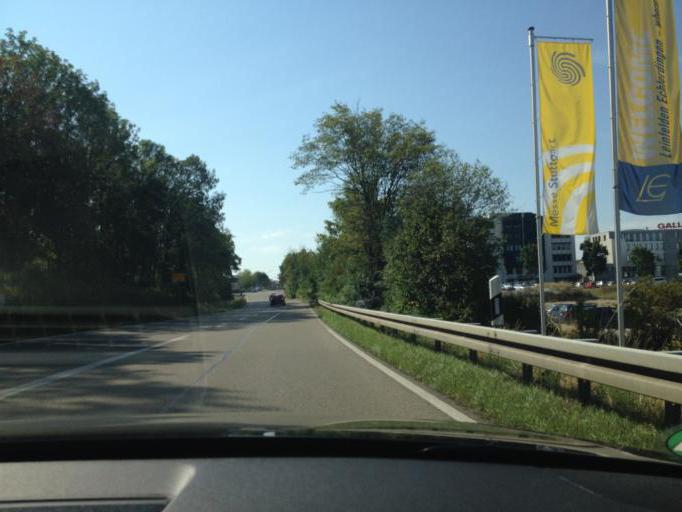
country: DE
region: Baden-Wuerttemberg
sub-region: Regierungsbezirk Stuttgart
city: Leinfelden-Echterdingen
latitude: 48.6993
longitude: 9.1665
